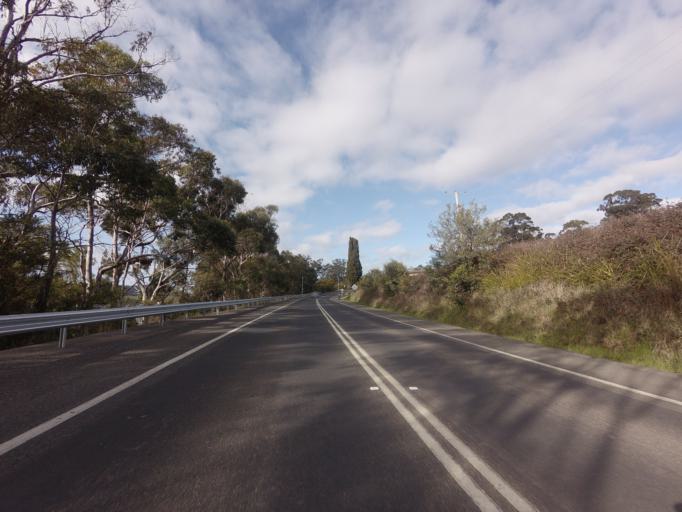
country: AU
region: Tasmania
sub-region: Huon Valley
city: Geeveston
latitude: -43.1561
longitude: 146.9805
